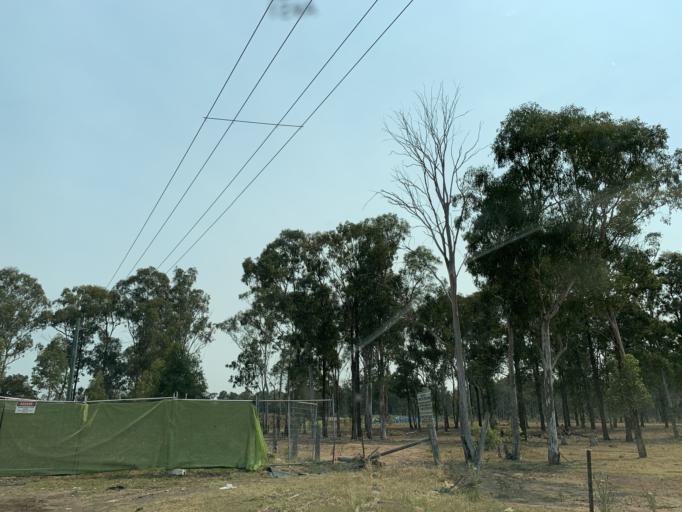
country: AU
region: New South Wales
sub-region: Blacktown
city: Blackett
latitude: -33.7198
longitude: 150.8195
